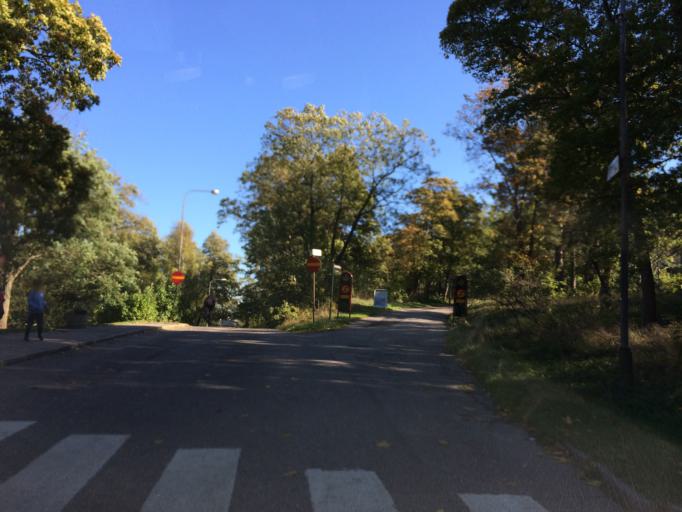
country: SE
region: Stockholm
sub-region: Nacka Kommun
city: Nacka
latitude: 59.3229
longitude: 18.1466
